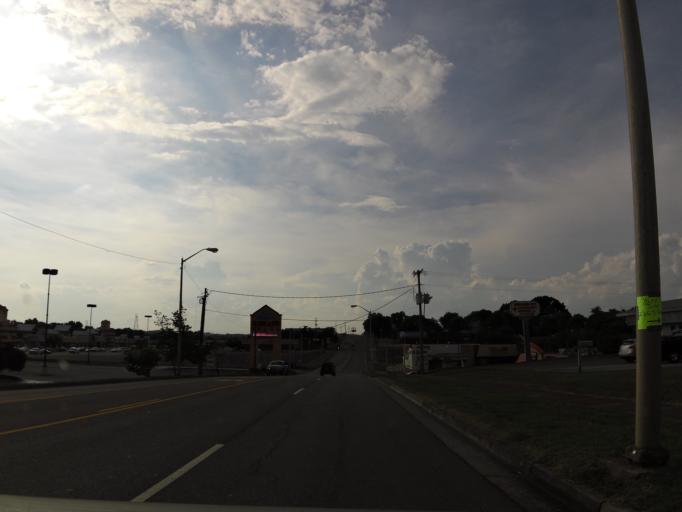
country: US
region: Tennessee
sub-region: Blount County
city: Maryville
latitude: 35.7607
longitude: -83.9765
